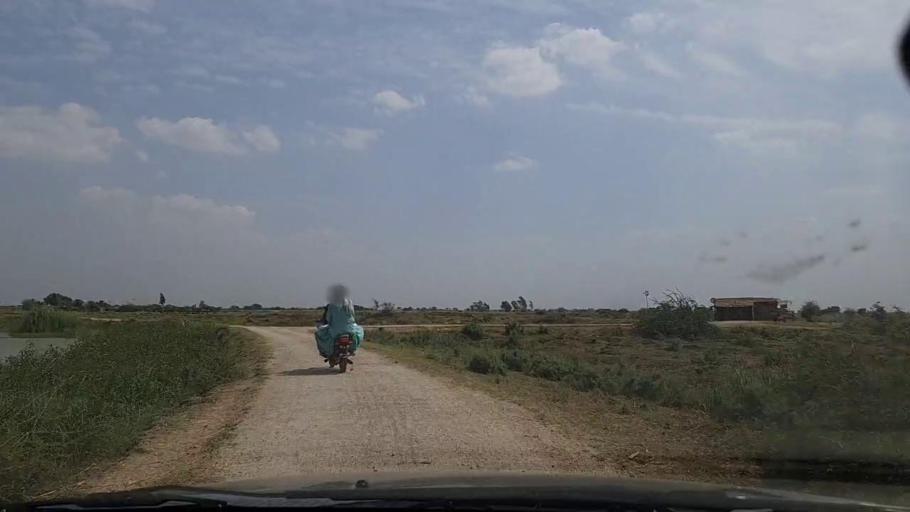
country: PK
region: Sindh
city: Mirpur Batoro
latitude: 24.5476
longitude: 68.2557
